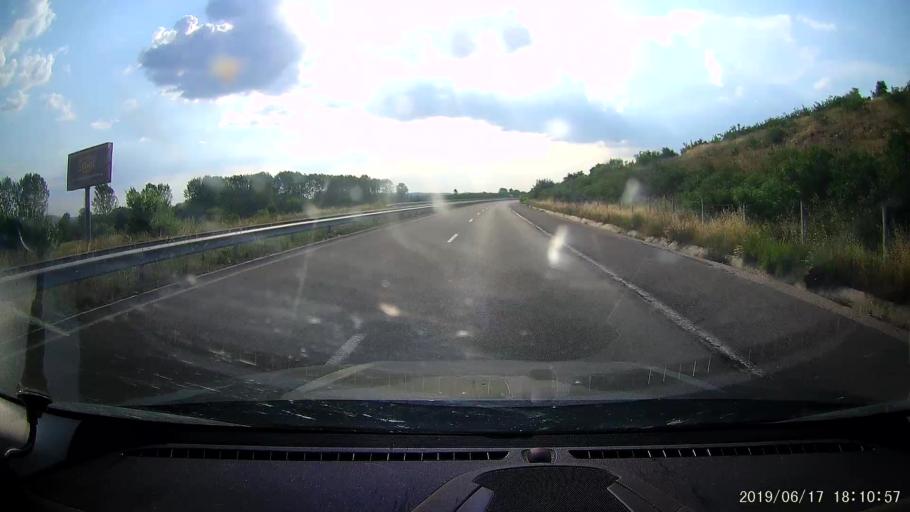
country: BG
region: Khaskovo
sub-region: Obshtina Lyubimets
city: Lyubimets
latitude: 41.8779
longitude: 26.0634
